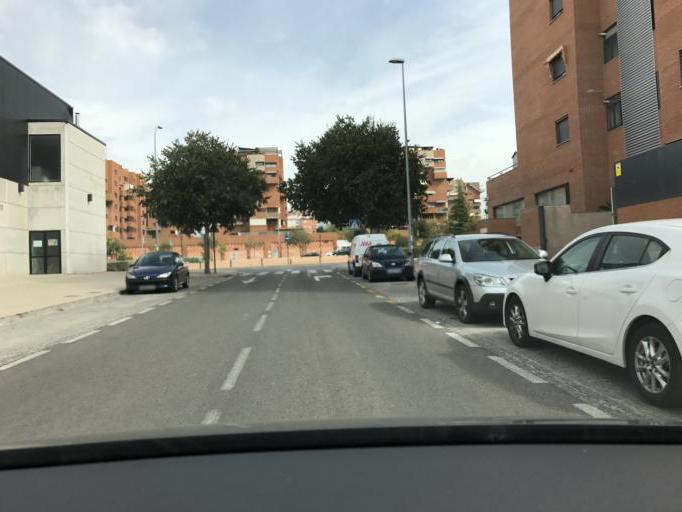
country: ES
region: Andalusia
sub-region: Provincia de Granada
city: Maracena
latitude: 37.2004
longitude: -3.6194
